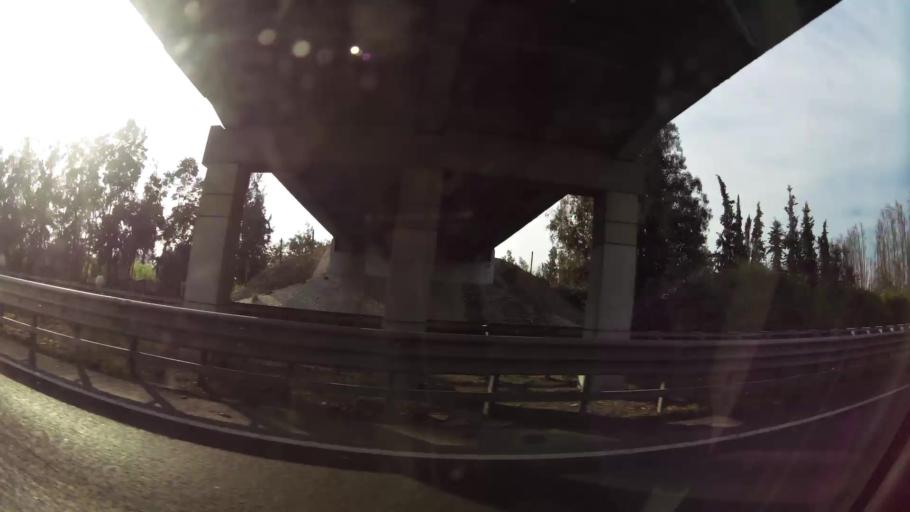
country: CL
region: Santiago Metropolitan
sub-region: Provincia de Talagante
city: Penaflor
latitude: -33.6230
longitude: -70.8608
